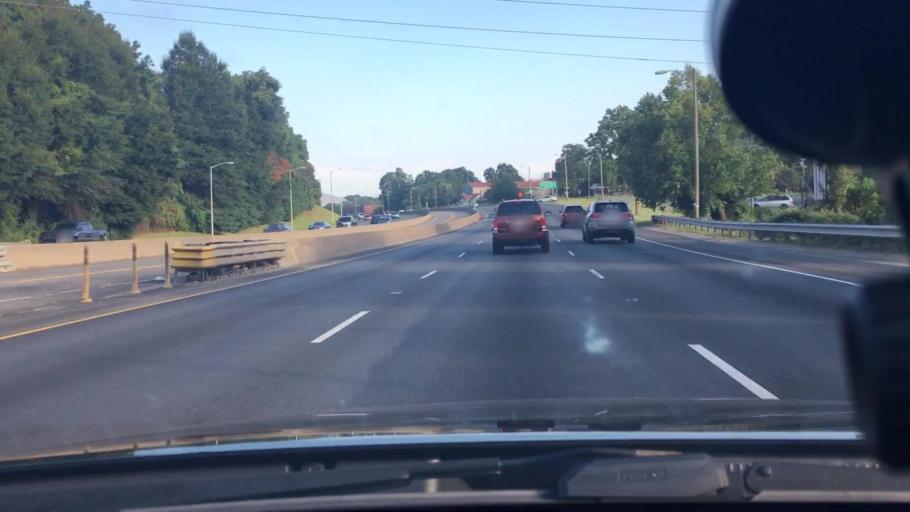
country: US
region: North Carolina
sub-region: Mecklenburg County
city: Charlotte
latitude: 35.2108
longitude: -80.8013
